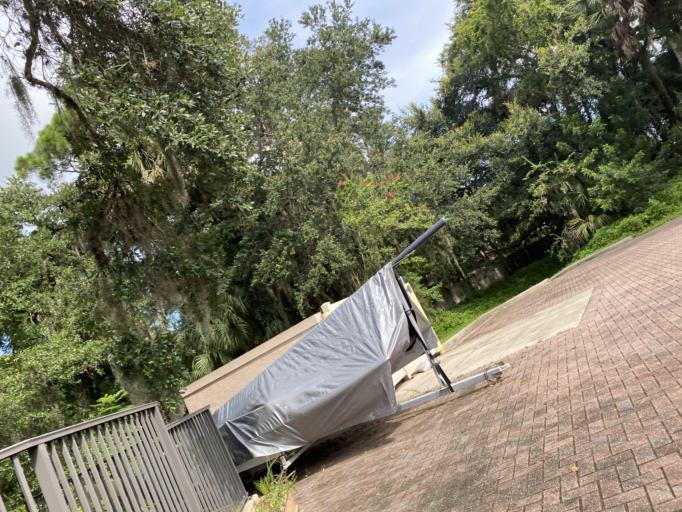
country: US
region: Florida
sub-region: Volusia County
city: Port Orange
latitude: 29.1350
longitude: -81.0006
